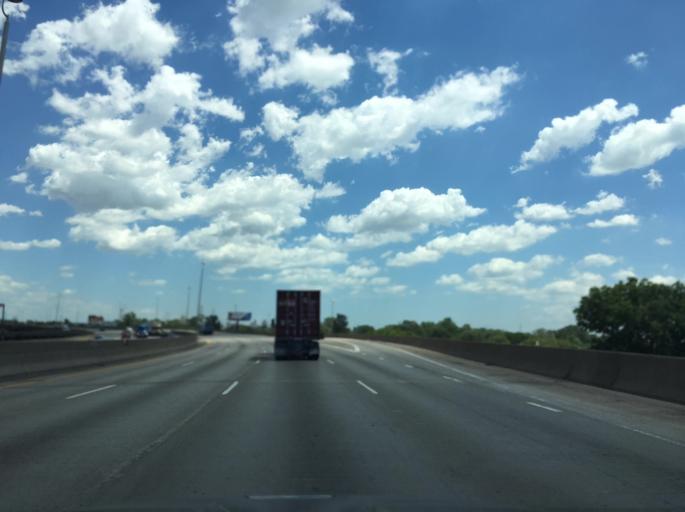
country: US
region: Michigan
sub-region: Wayne County
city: River Rouge
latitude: 42.2901
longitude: -83.1313
